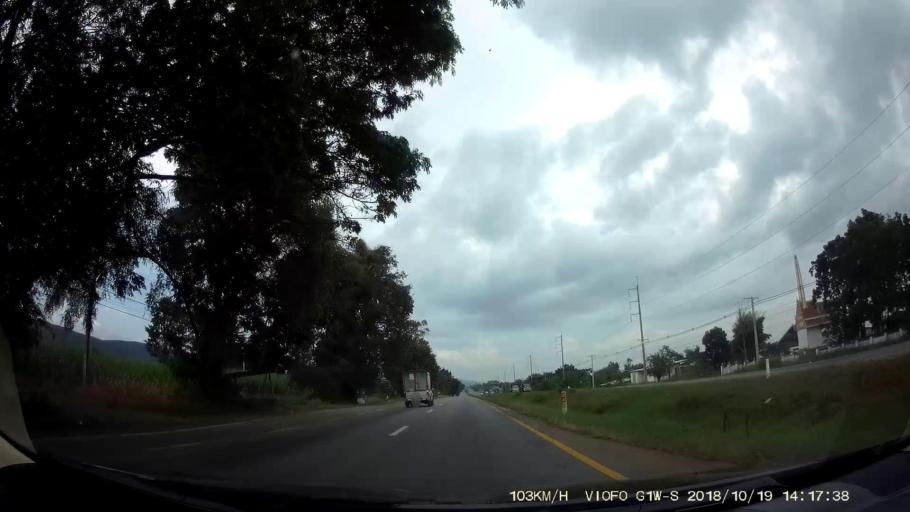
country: TH
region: Chaiyaphum
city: Khon Sawan
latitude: 16.0057
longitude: 102.2269
